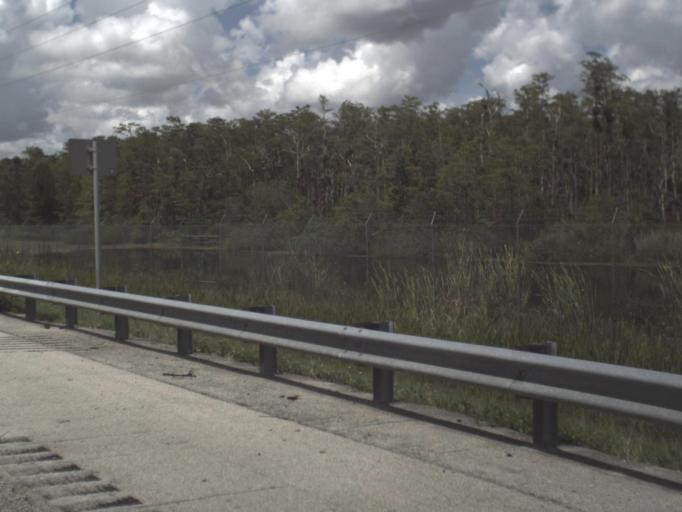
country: US
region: Florida
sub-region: Collier County
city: Immokalee
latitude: 26.1701
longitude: -81.0067
